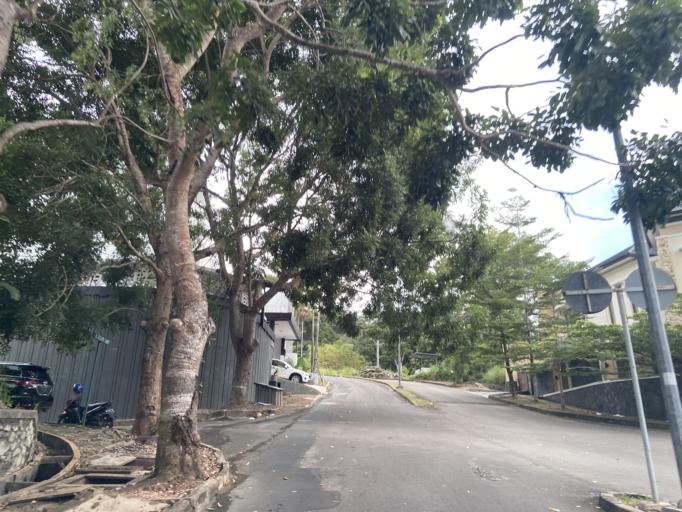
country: SG
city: Singapore
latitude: 1.1015
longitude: 104.0270
